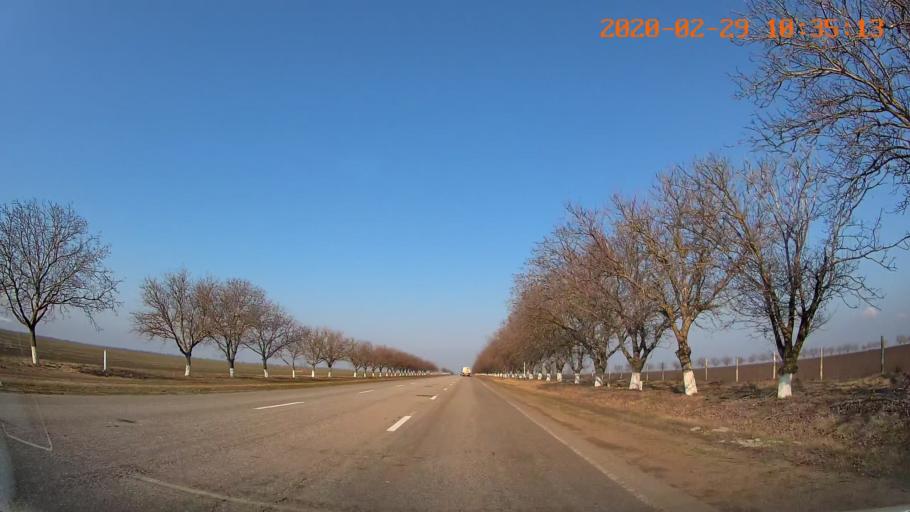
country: MD
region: Anenii Noi
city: Varnita
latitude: 46.9835
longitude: 29.5238
